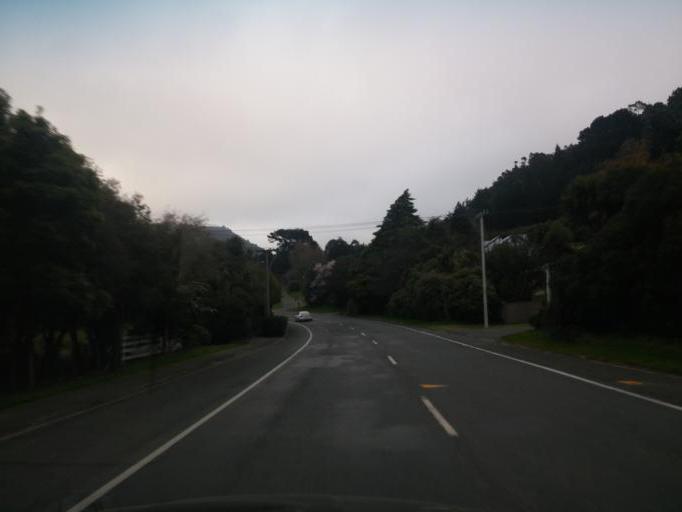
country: NZ
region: Wellington
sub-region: Upper Hutt City
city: Upper Hutt
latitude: -41.1155
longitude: 175.3182
